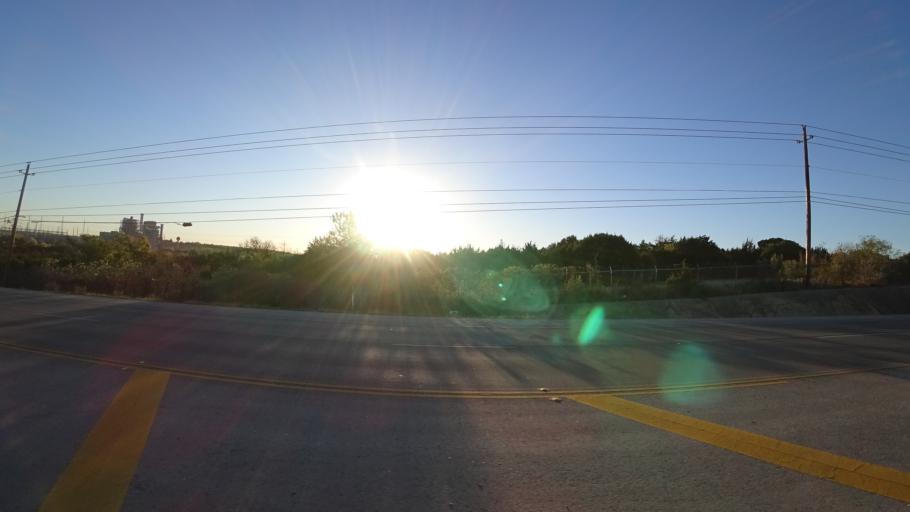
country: US
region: Texas
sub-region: Travis County
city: Hornsby Bend
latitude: 30.3016
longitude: -97.6213
